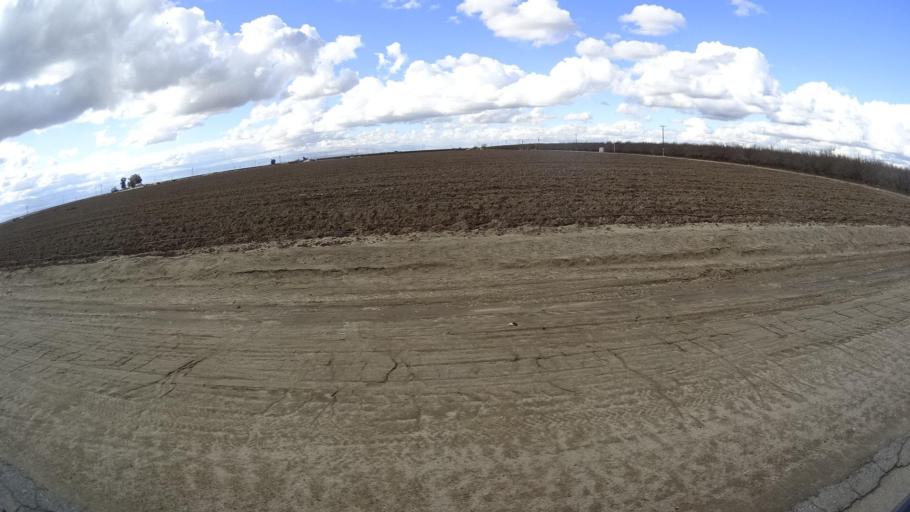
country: US
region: California
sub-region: Kern County
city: Greenfield
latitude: 35.2155
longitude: -119.0569
